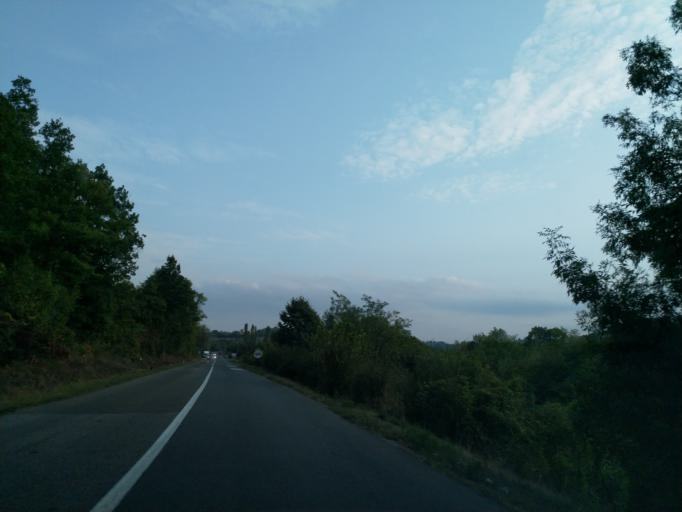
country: RS
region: Central Serbia
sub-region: Sumadijski Okrug
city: Topola
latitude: 44.2171
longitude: 20.7222
